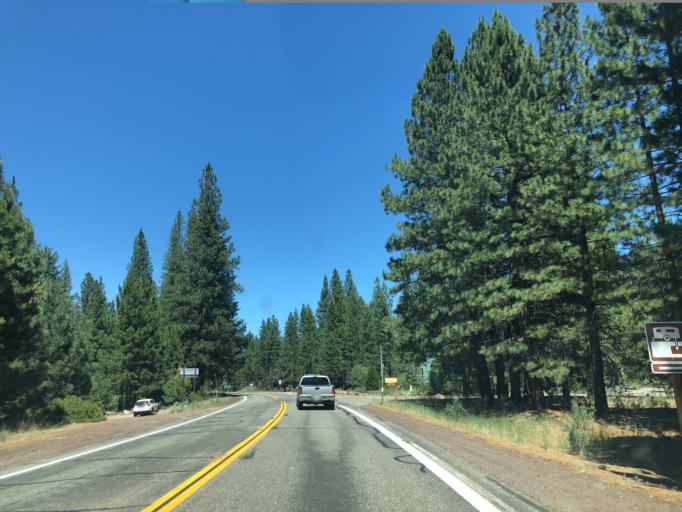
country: US
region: California
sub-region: Shasta County
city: Burney
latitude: 40.6785
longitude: -121.4262
